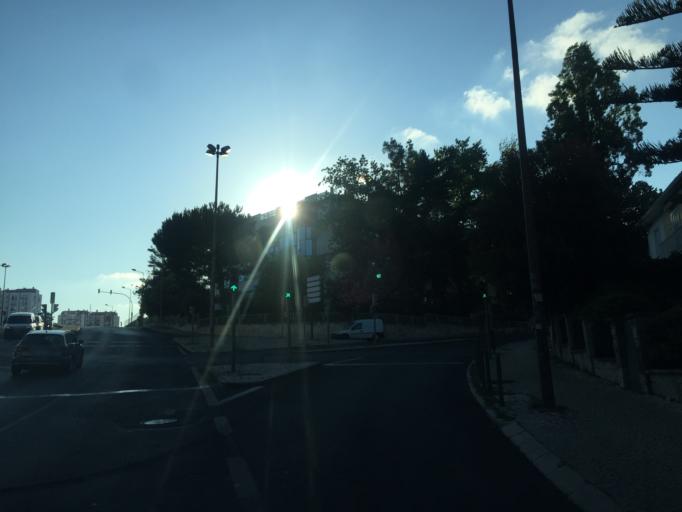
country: PT
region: Lisbon
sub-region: Odivelas
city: Pontinha
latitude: 38.7454
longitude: -9.2036
